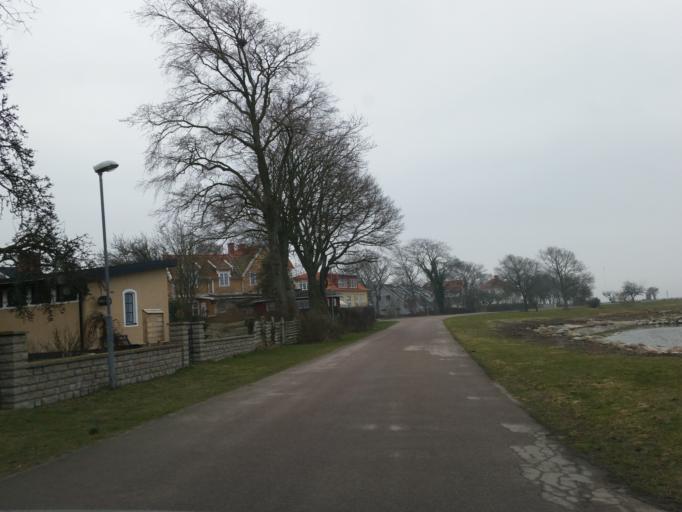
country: SE
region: Kalmar
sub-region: Morbylanga Kommun
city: Moerbylanga
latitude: 56.5251
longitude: 16.3717
